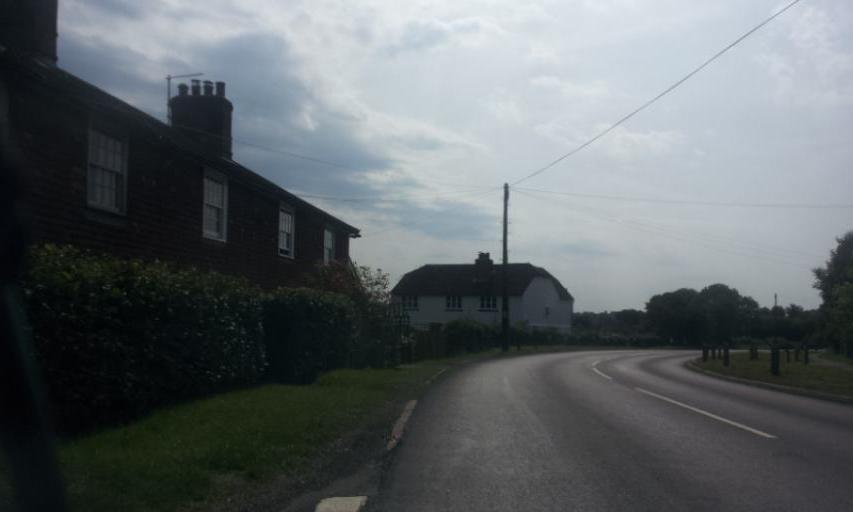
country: GB
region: England
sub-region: Kent
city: Paddock Wood
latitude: 51.1557
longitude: 0.3774
